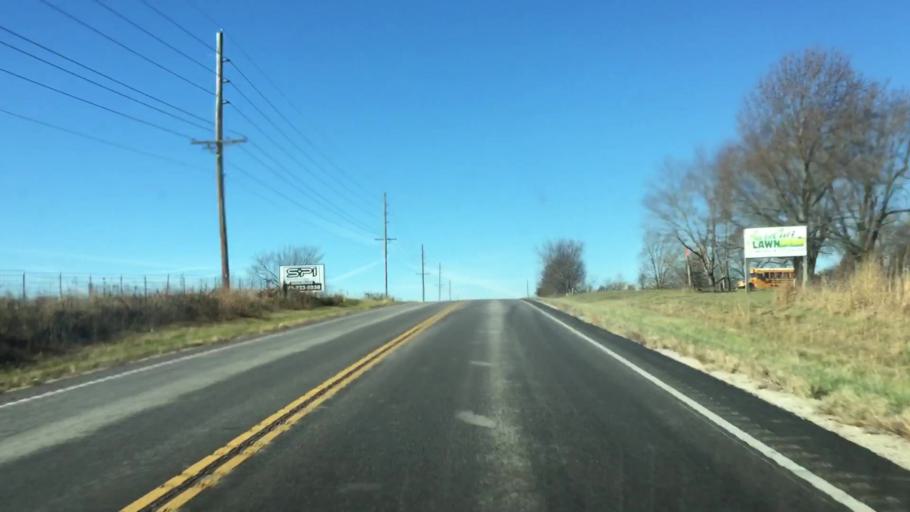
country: US
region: Missouri
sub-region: Miller County
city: Eldon
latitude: 38.3738
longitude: -92.6288
